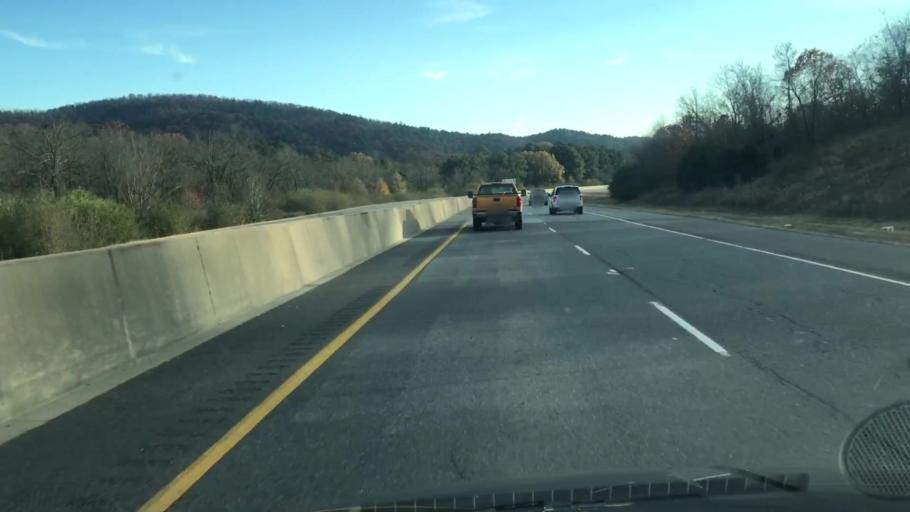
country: US
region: Arkansas
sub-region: Garland County
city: Hot Springs
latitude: 34.4965
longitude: -92.9758
